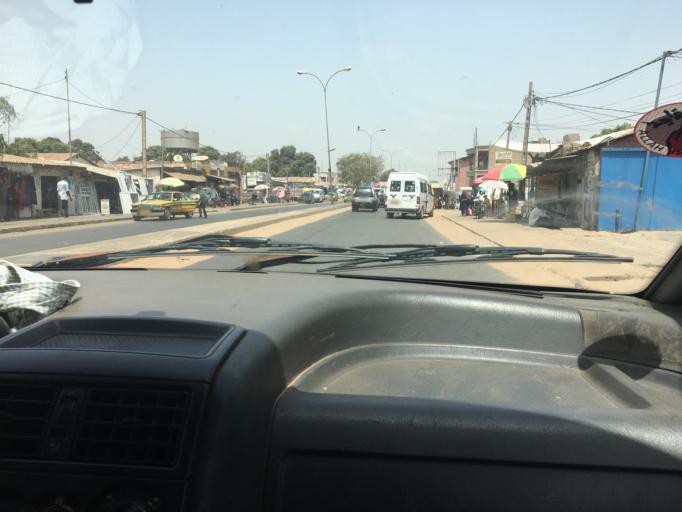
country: GM
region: Western
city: Abuko
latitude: 13.4110
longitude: -16.6707
